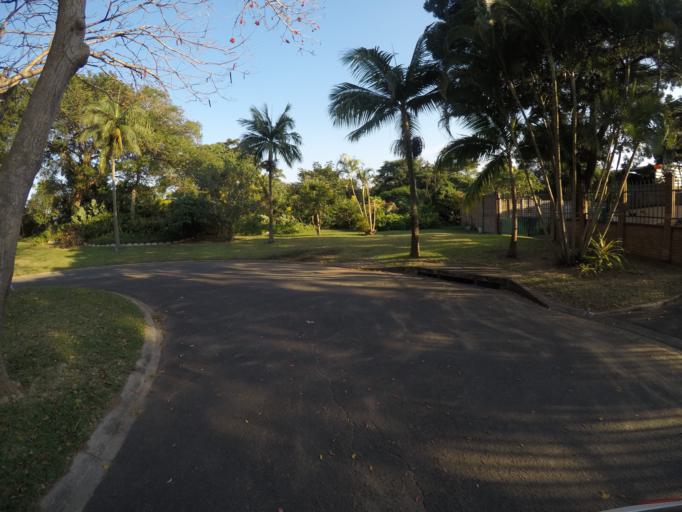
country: ZA
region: KwaZulu-Natal
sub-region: uThungulu District Municipality
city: Richards Bay
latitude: -28.7756
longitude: 32.1144
